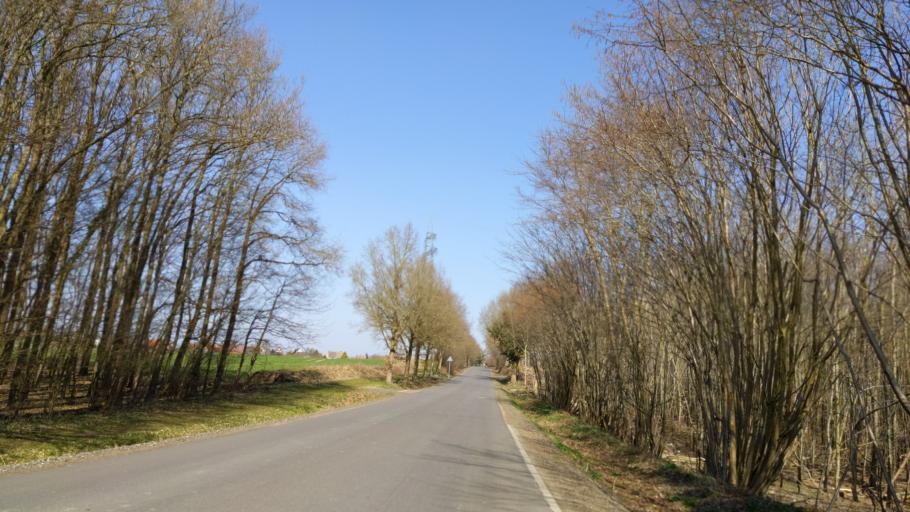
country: DE
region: Schleswig-Holstein
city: Susel
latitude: 54.0963
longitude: 10.7091
